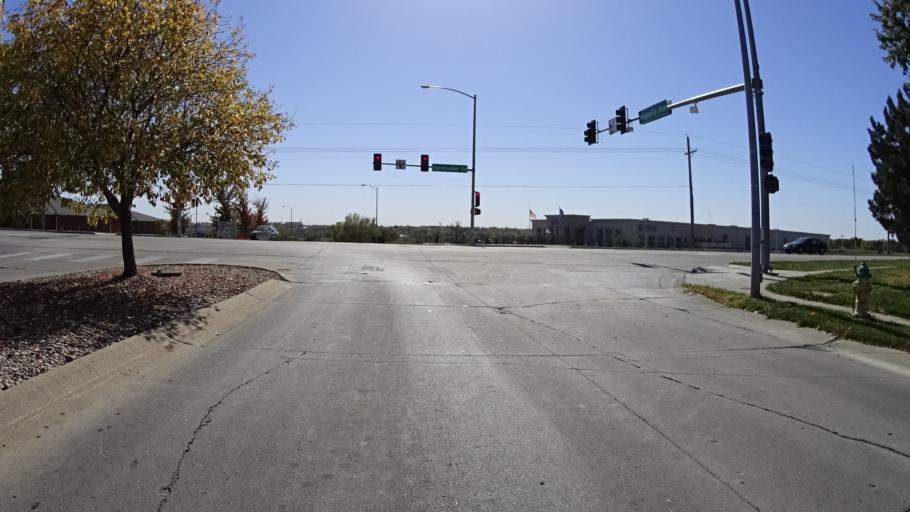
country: US
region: Nebraska
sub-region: Sarpy County
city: Papillion
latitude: 41.1620
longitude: -96.0278
